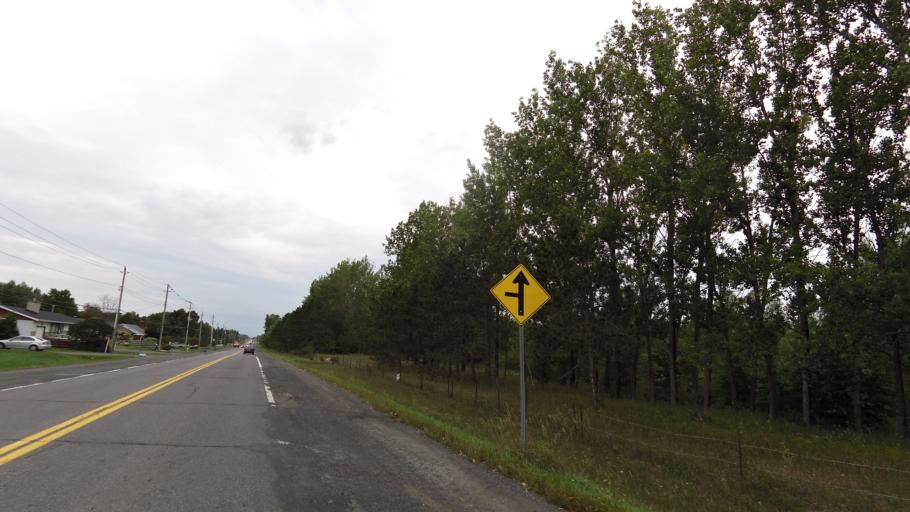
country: CA
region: Ontario
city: Ottawa
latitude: 45.2745
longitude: -75.5827
